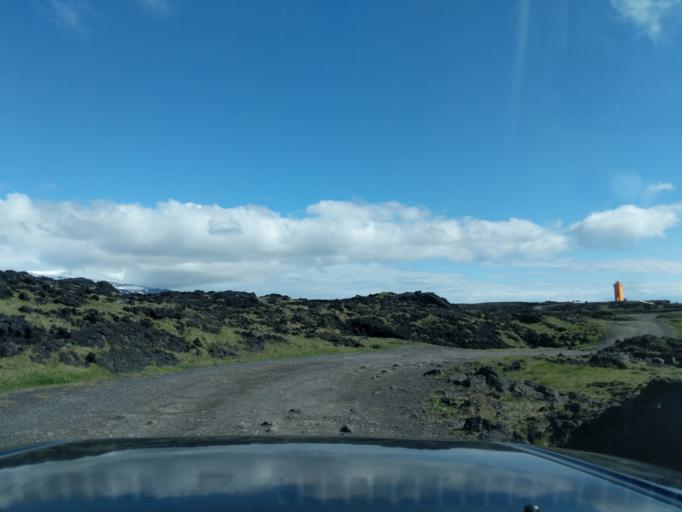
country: IS
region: West
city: Olafsvik
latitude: 64.8674
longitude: -24.0396
